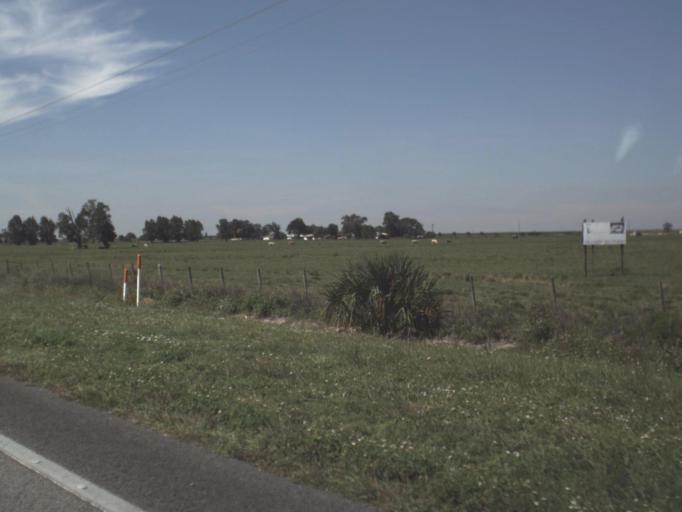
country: US
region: Florida
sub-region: Hendry County
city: Harlem
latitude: 26.7542
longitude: -81.0090
